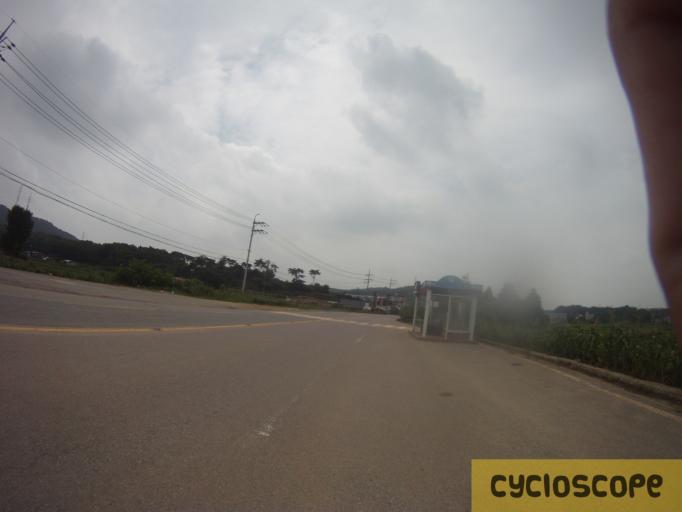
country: KR
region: Gyeonggi-do
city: Hwaseong-si
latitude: 37.1446
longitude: 126.8721
